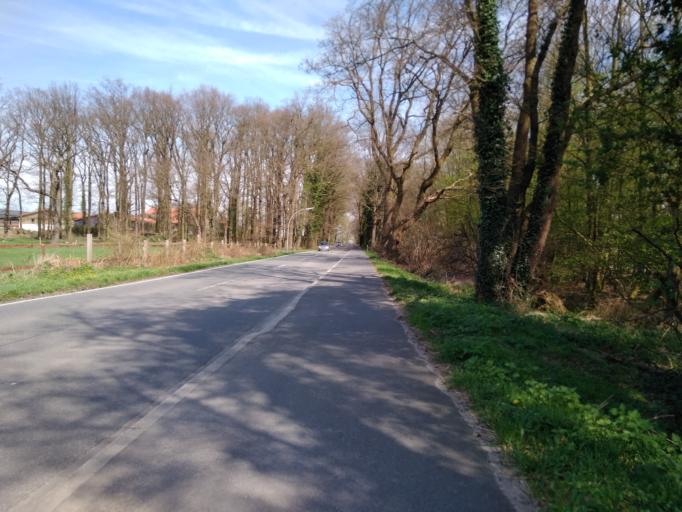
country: DE
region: North Rhine-Westphalia
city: Dorsten
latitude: 51.6529
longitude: 6.9388
